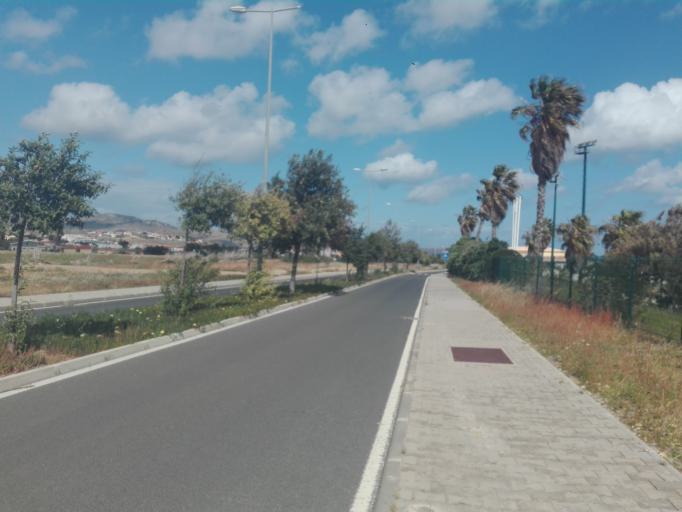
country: PT
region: Madeira
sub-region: Porto Santo
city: Vila de Porto Santo
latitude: 33.0470
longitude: -16.3574
